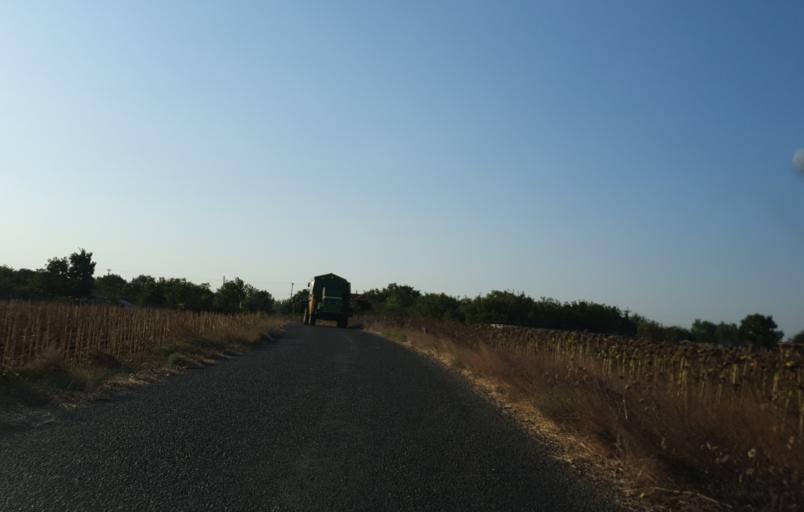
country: TR
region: Tekirdag
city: Beyazkoy
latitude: 41.4311
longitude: 27.7563
